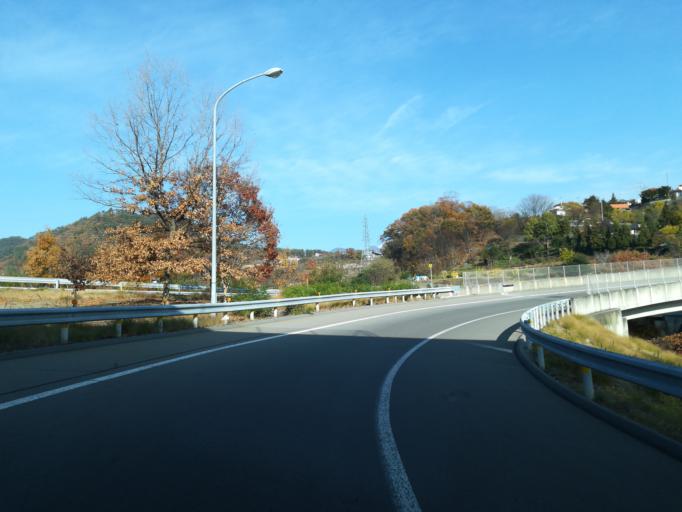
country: JP
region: Nagano
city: Ueda
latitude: 36.4140
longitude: 138.2836
